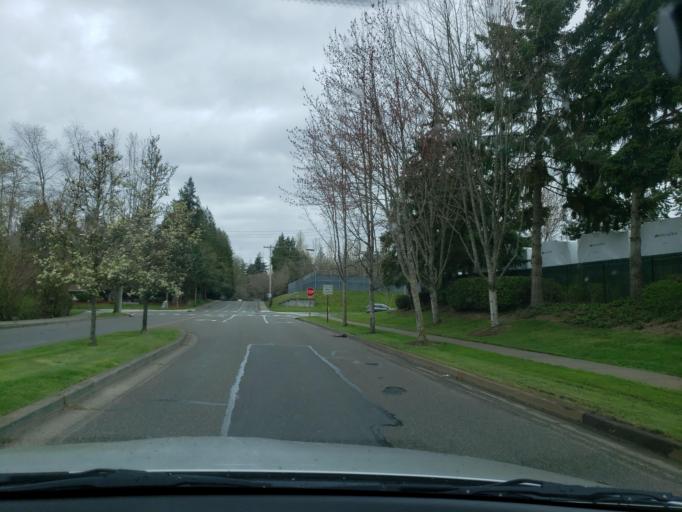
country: US
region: Washington
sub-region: Snohomish County
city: Mukilteo
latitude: 47.8944
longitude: -122.3001
